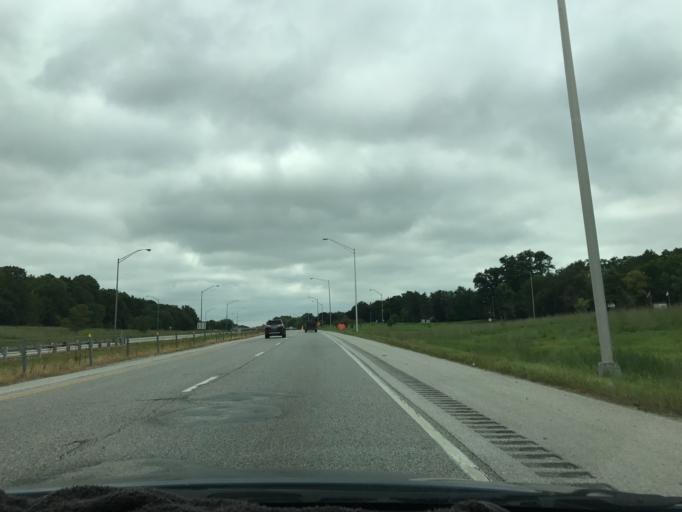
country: US
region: Illinois
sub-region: Rock Island County
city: Moline
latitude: 41.4908
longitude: -90.5045
